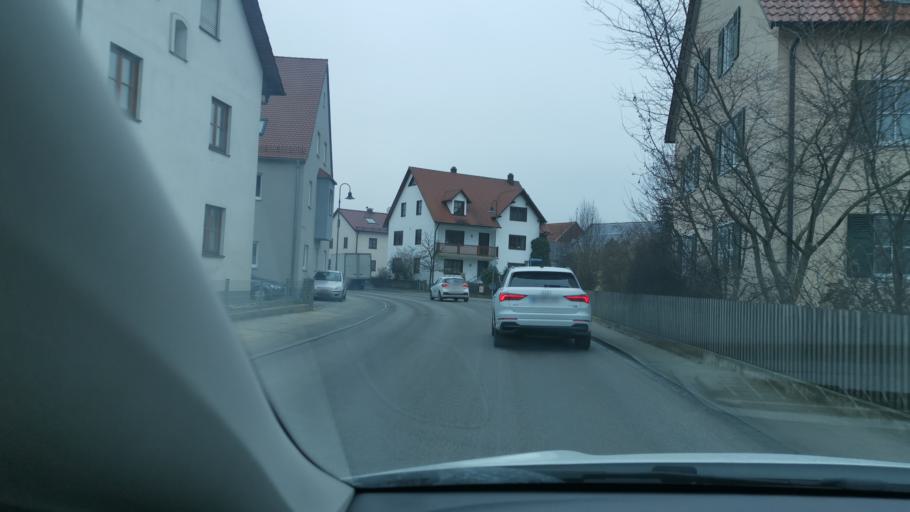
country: DE
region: Bavaria
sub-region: Swabia
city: Thierhaupten
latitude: 48.5651
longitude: 10.9098
